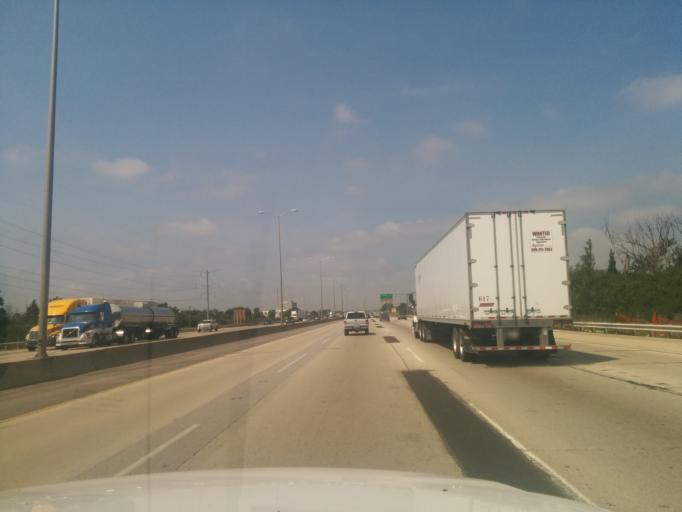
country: US
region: Illinois
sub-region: Cook County
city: Hoffman Estates
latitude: 42.0615
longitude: -88.0595
